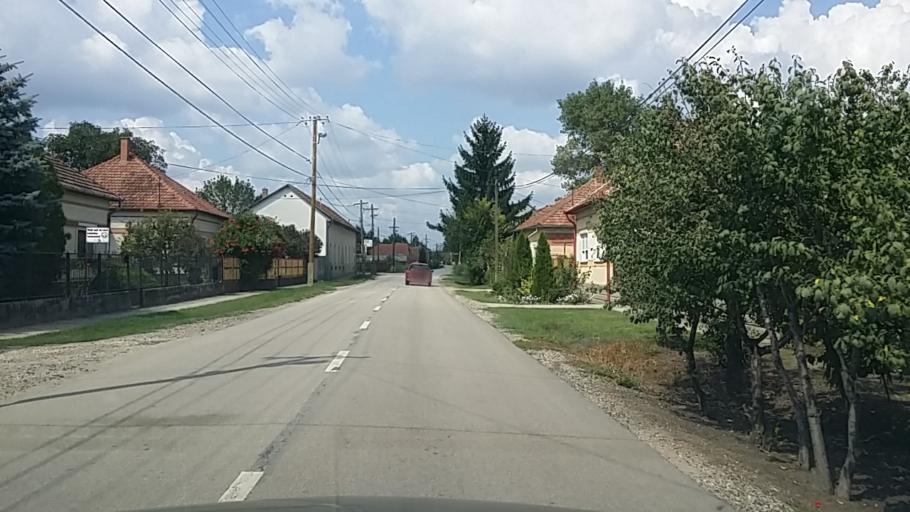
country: HU
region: Bacs-Kiskun
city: Tiszaalpar
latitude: 46.8048
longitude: 20.0065
